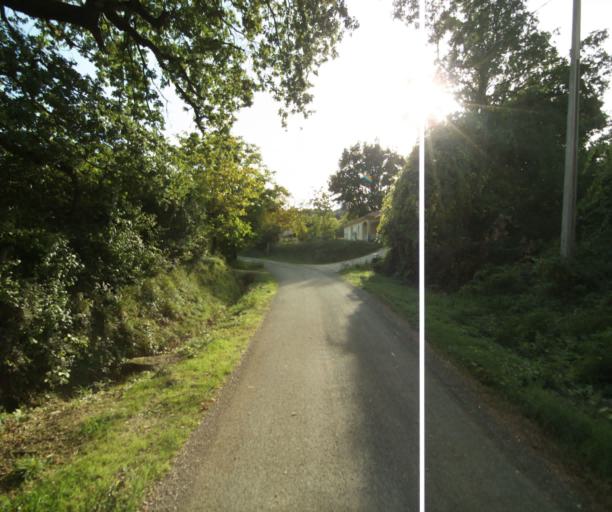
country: FR
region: Midi-Pyrenees
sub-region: Departement du Gers
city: Gondrin
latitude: 43.9087
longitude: 0.2448
